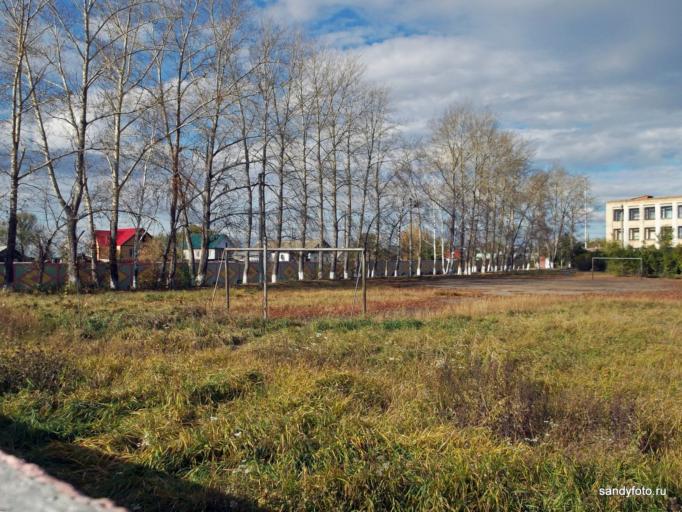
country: RU
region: Chelyabinsk
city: Troitsk
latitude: 54.0894
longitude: 61.5894
